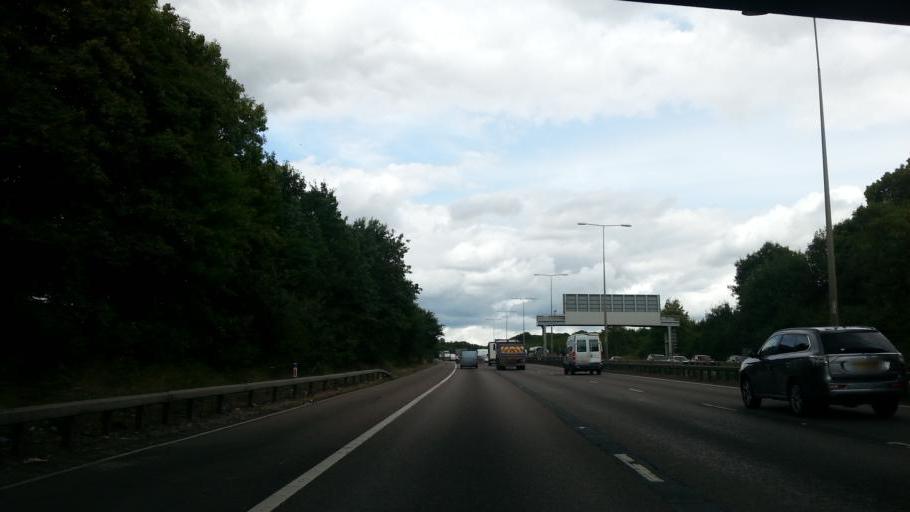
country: GB
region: England
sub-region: Essex
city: Epping
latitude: 51.6933
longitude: 0.1385
